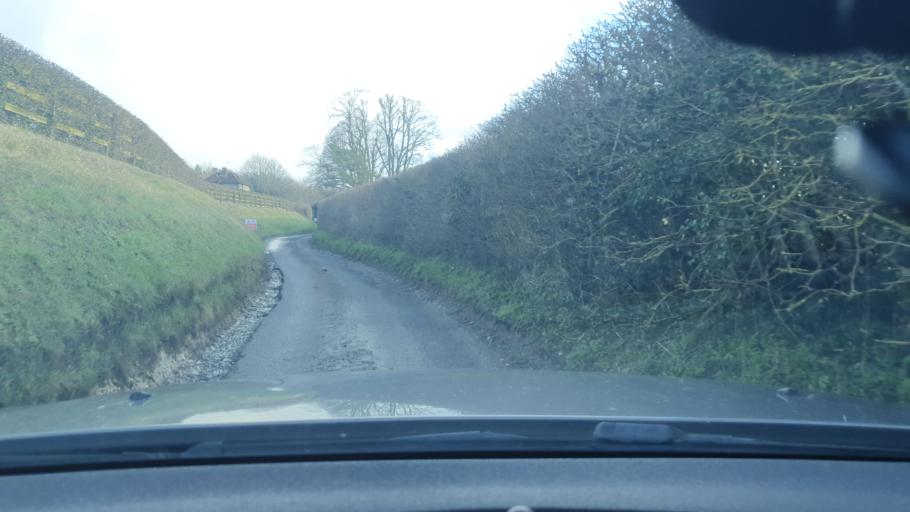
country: GB
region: England
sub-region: Wokingham
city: Wargrave
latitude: 51.5285
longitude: -0.8433
